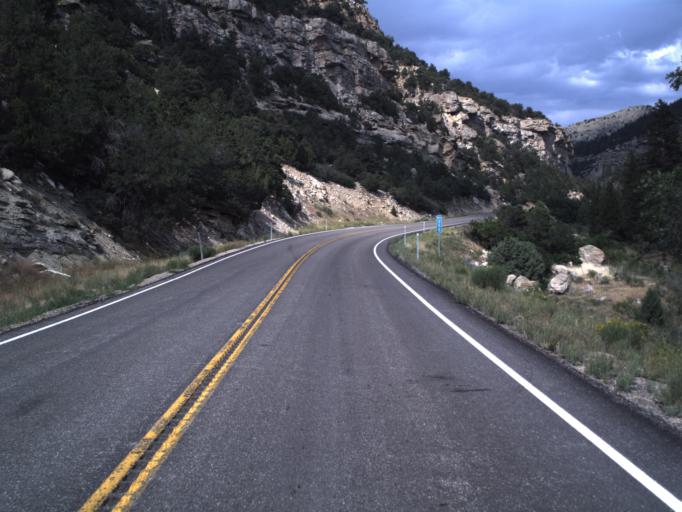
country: US
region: Utah
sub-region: Carbon County
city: Helper
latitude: 39.7561
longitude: -110.8234
